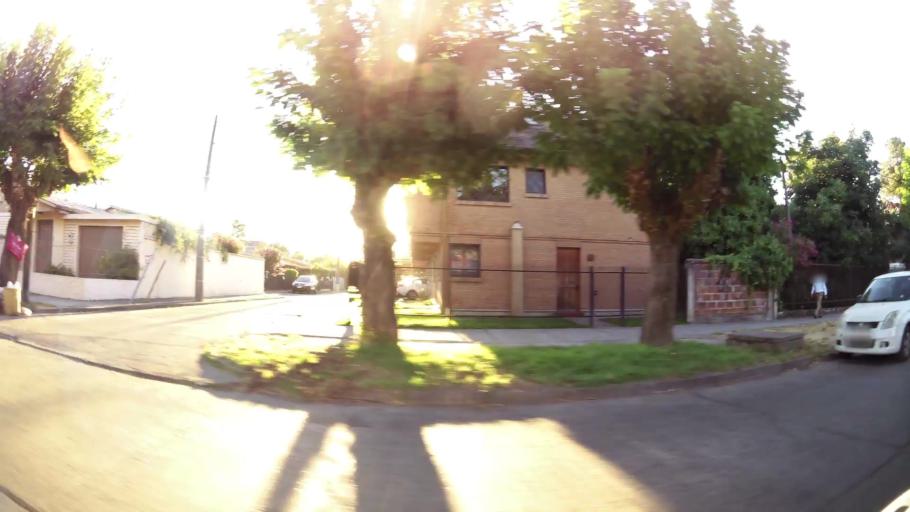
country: CL
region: Maule
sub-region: Provincia de Curico
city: Curico
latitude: -34.9915
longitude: -71.2393
